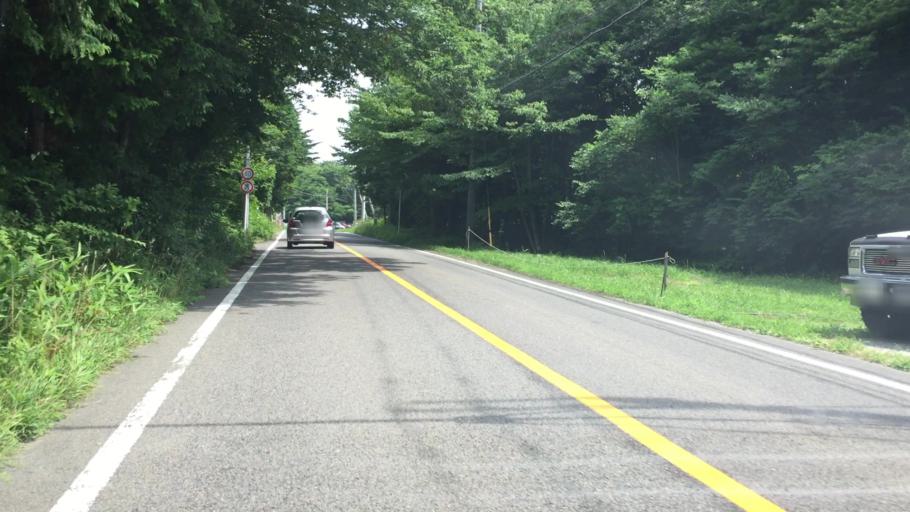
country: JP
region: Tochigi
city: Kuroiso
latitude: 37.0475
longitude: 139.9375
